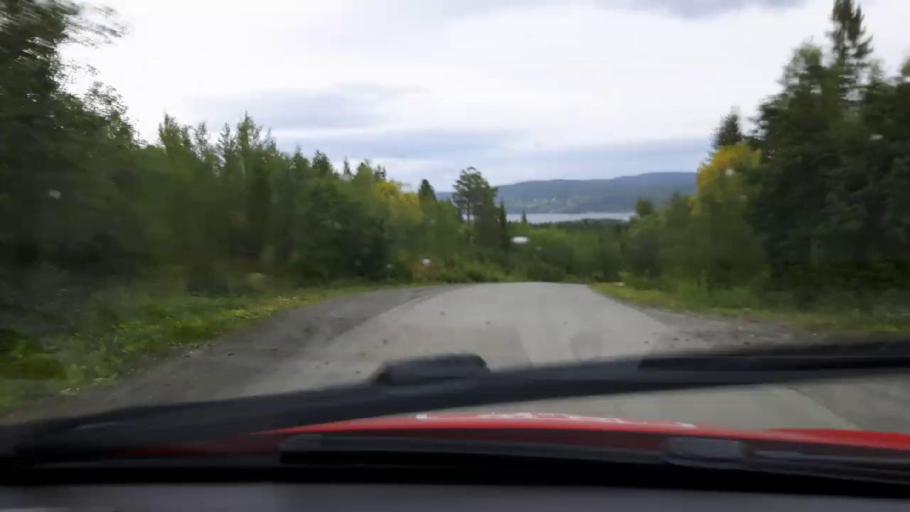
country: SE
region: Jaemtland
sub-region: Are Kommun
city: Are
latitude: 63.4357
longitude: 13.2109
